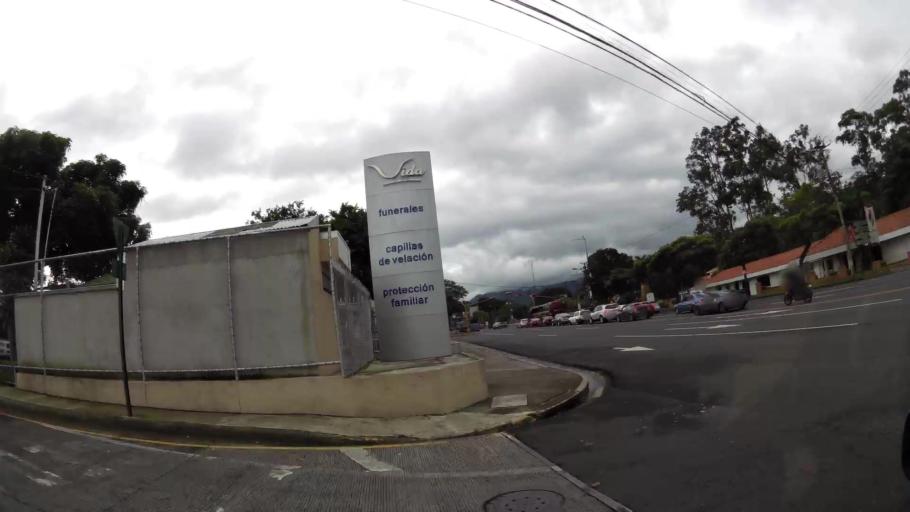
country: CR
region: San Jose
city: San Jose
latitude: 9.9367
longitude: -84.0981
